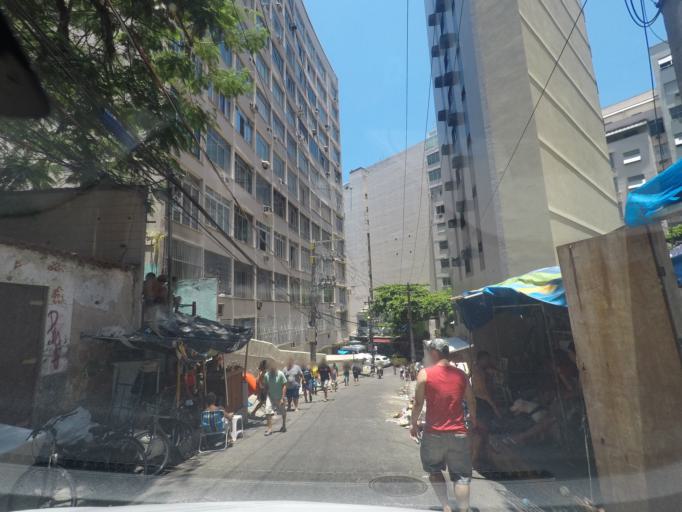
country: BR
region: Rio de Janeiro
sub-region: Rio De Janeiro
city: Rio de Janeiro
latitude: -22.9806
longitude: -43.1919
